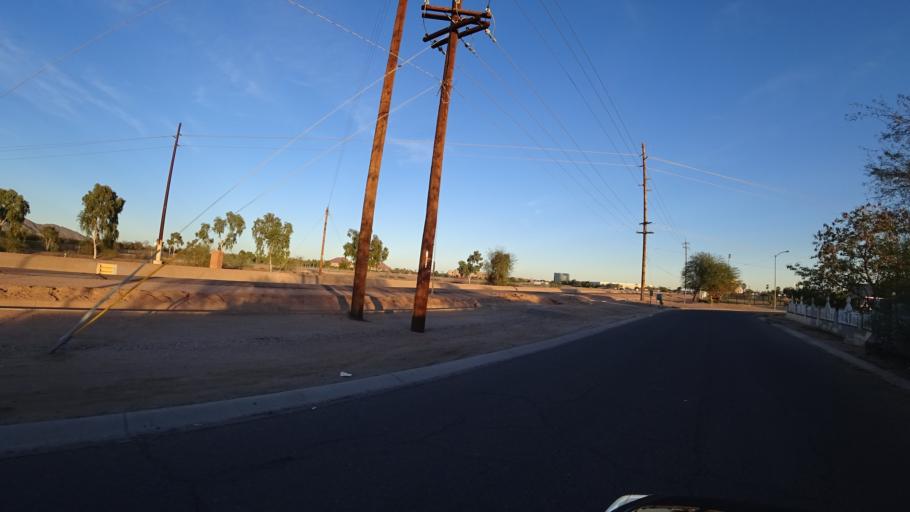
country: US
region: Arizona
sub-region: Maricopa County
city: Phoenix
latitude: 33.4572
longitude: -112.0047
